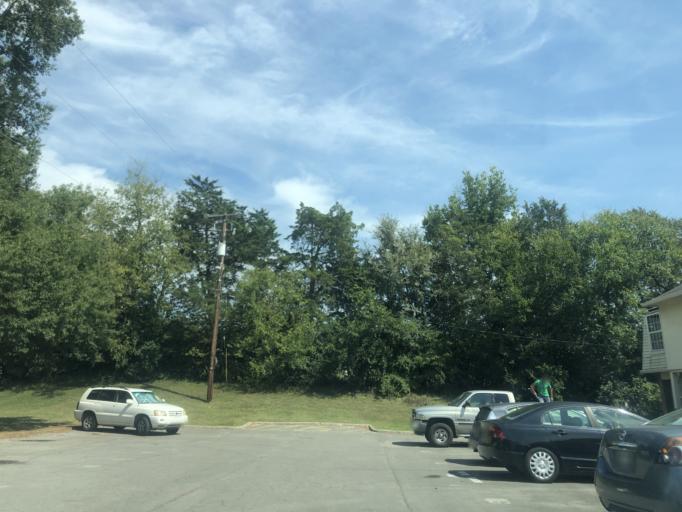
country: US
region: Tennessee
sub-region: Williamson County
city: Brentwood Estates
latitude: 36.0471
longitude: -86.7049
